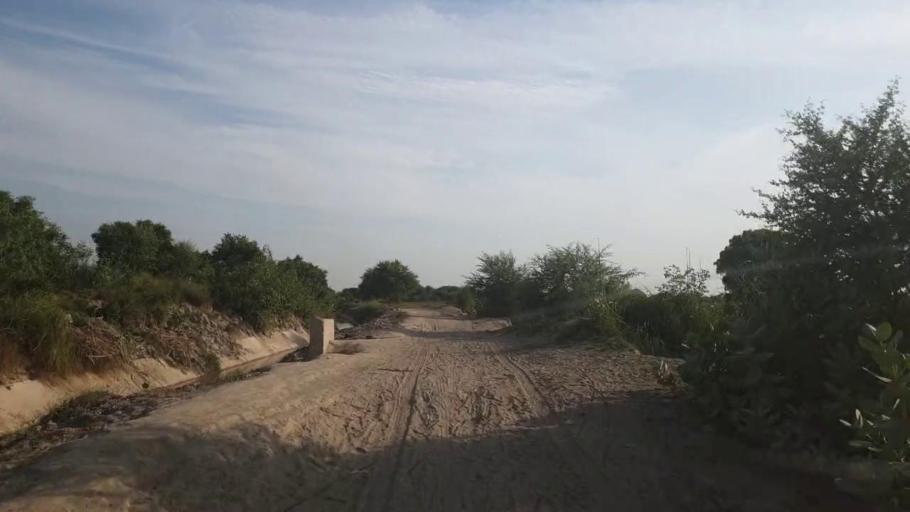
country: PK
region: Sindh
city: Tando Muhammad Khan
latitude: 25.2294
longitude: 68.5358
